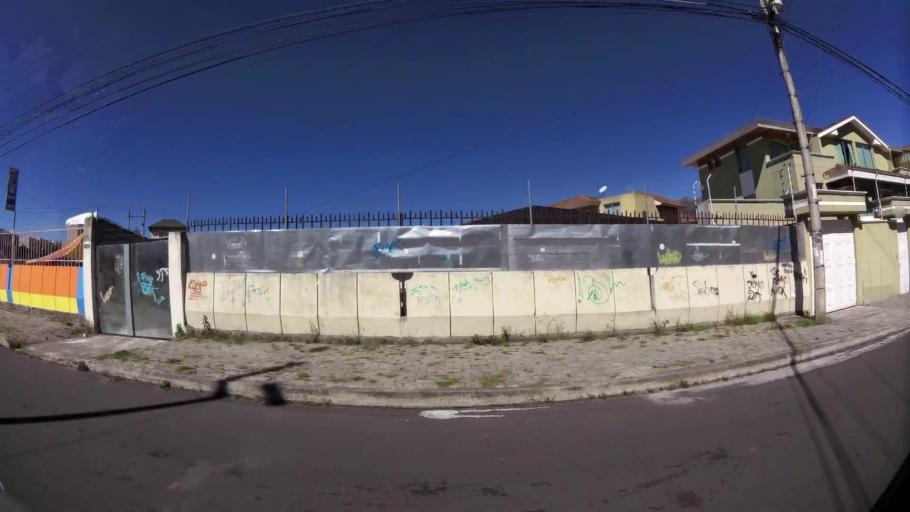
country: EC
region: Pichincha
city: Quito
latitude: -0.1261
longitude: -78.4745
